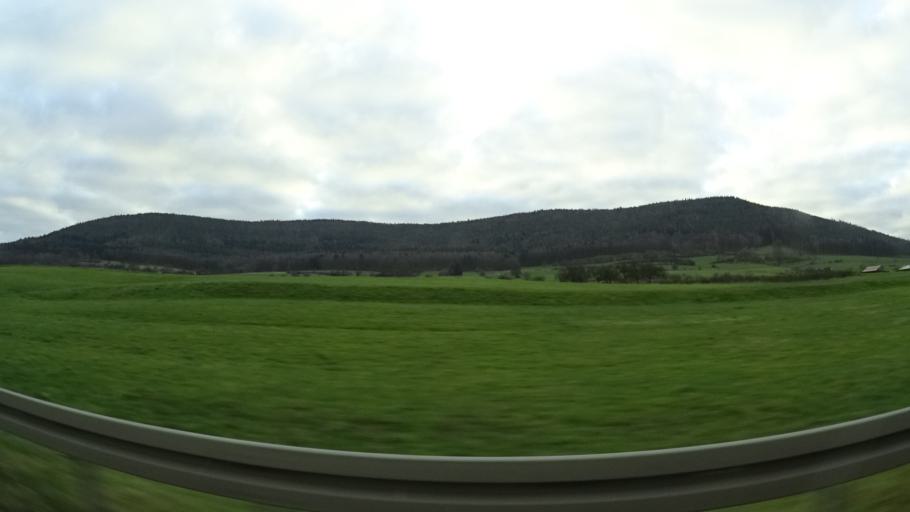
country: DE
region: Bavaria
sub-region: Regierungsbezirk Unterfranken
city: Burgstadt
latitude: 49.7349
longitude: 9.2834
